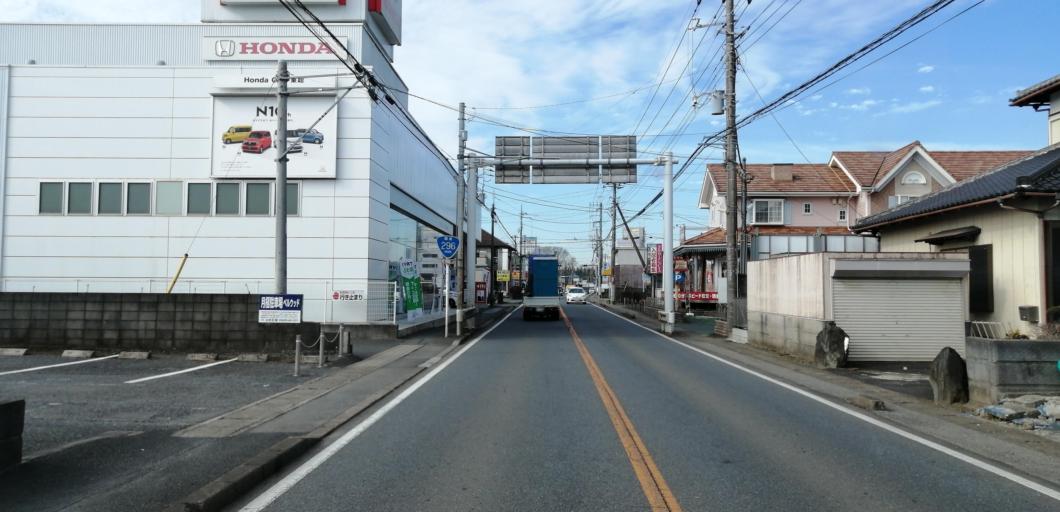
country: JP
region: Chiba
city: Narita
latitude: 35.7363
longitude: 140.3265
